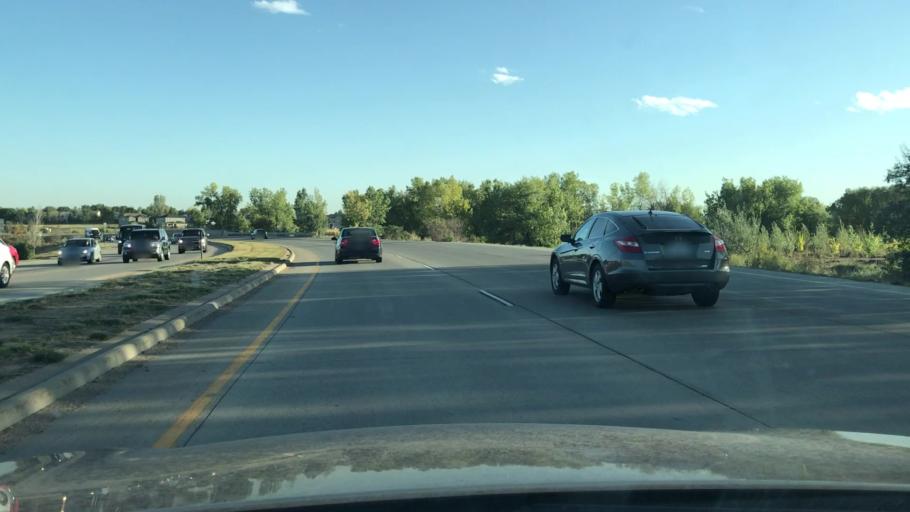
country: US
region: Colorado
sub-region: Boulder County
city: Lafayette
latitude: 39.9817
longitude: -105.0984
